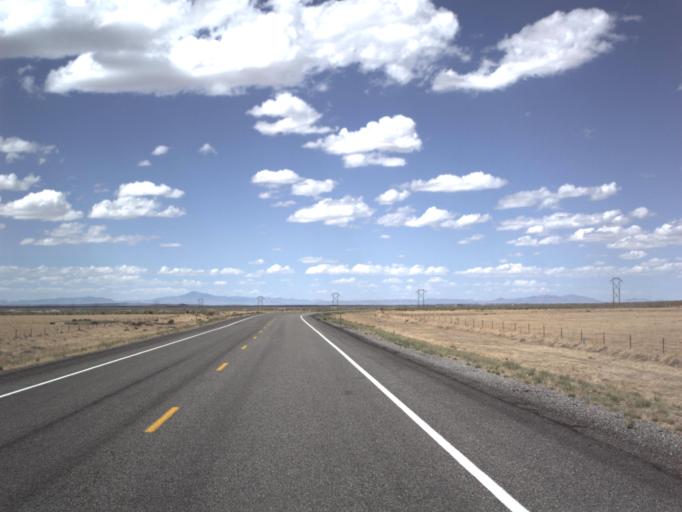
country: US
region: Utah
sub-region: Millard County
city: Fillmore
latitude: 39.1493
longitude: -112.3941
